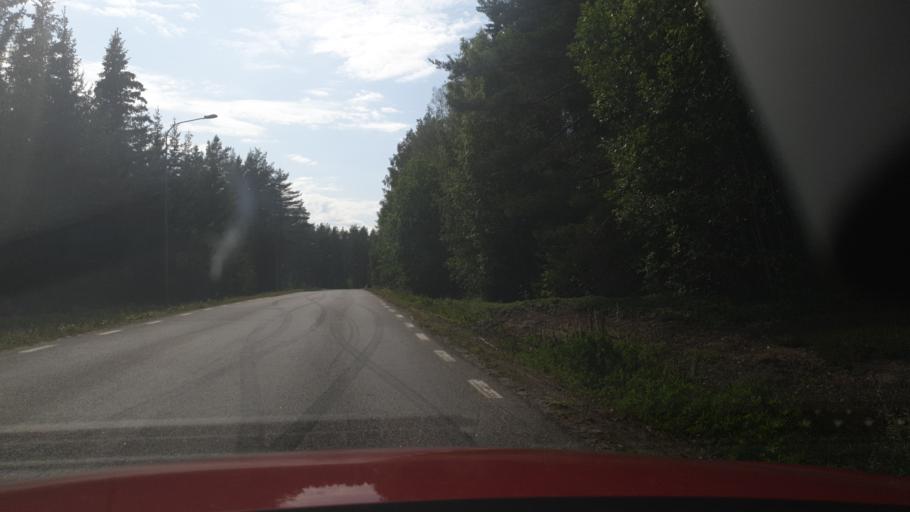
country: SE
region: Vaesternorrland
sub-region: Sundsvalls Kommun
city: Njurundabommen
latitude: 62.0357
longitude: 17.3394
